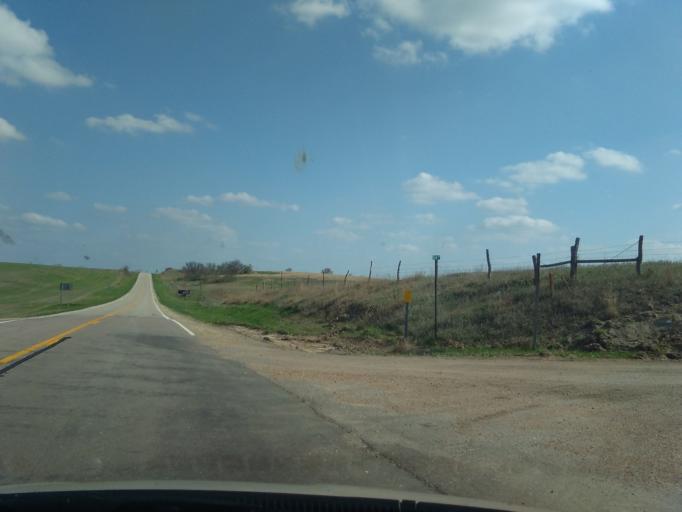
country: US
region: Nebraska
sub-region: Webster County
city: Red Cloud
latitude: 40.0026
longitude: -98.3296
